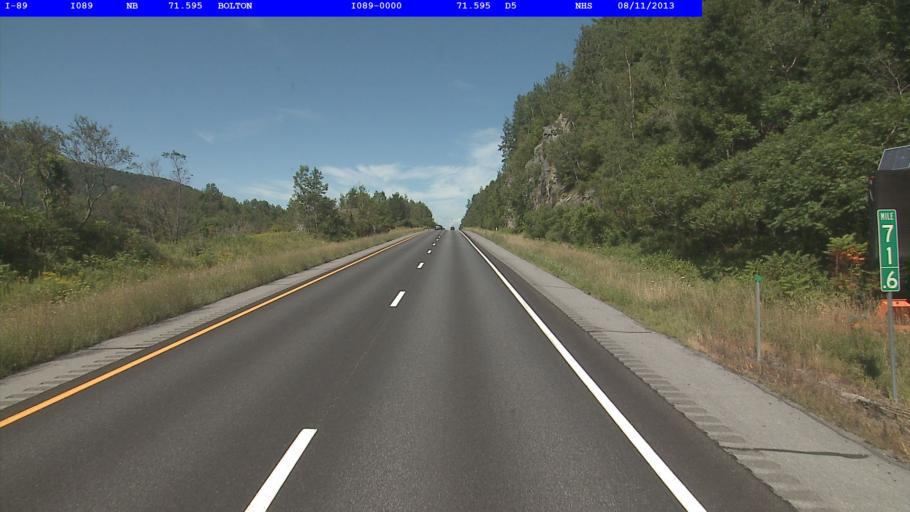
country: US
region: Vermont
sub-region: Washington County
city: Waterbury
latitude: 44.3782
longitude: -72.8979
